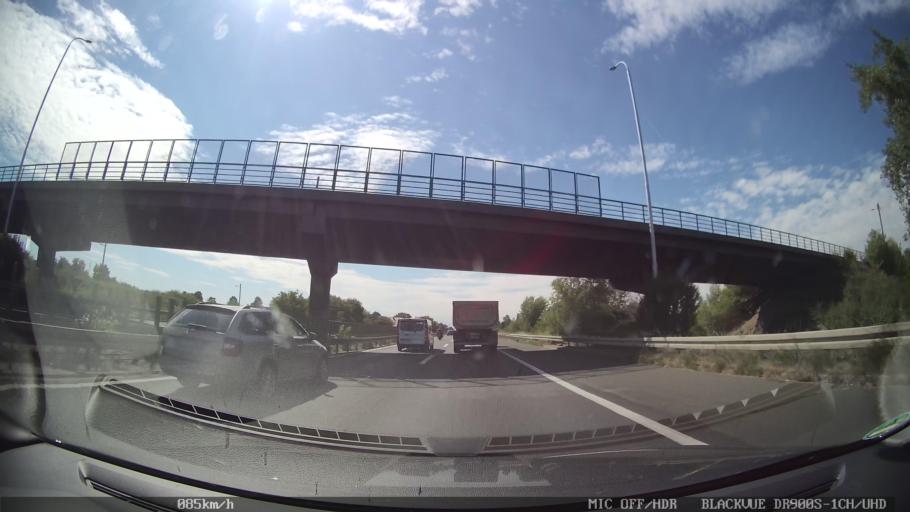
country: HR
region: Grad Zagreb
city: Novi Zagreb
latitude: 45.7507
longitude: 15.9642
